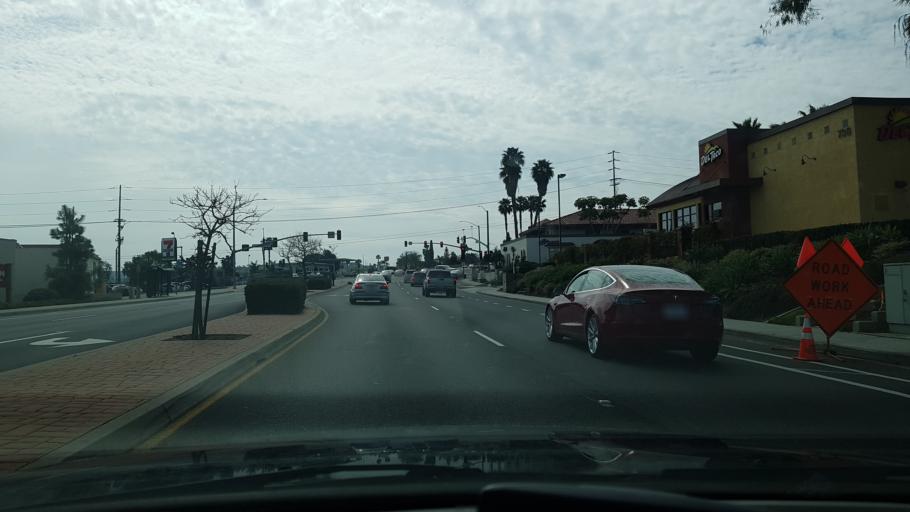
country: US
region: California
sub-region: San Diego County
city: Lake San Marcos
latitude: 33.1325
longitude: -117.2076
